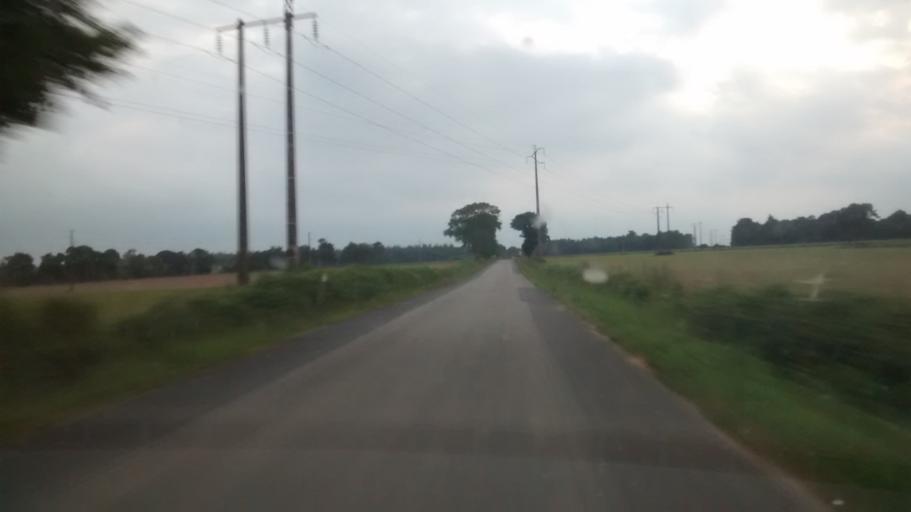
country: FR
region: Brittany
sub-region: Departement du Morbihan
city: Saint-Martin-sur-Oust
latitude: 47.7311
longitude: -2.3034
